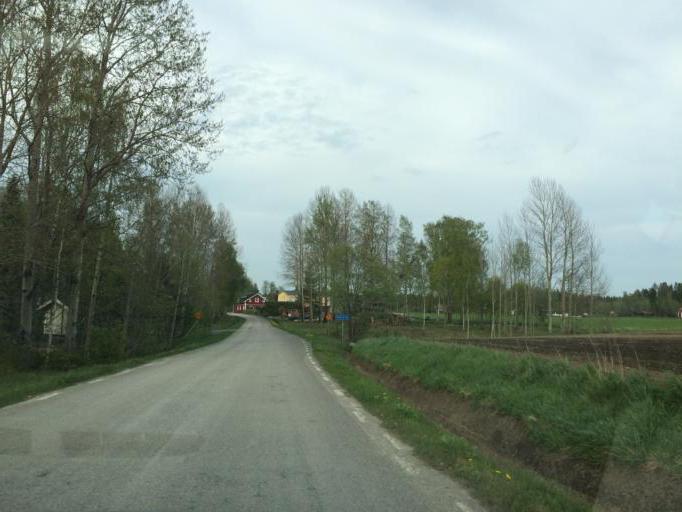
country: SE
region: Vaestmanland
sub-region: Kopings Kommun
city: Koping
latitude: 59.6159
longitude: 16.0331
